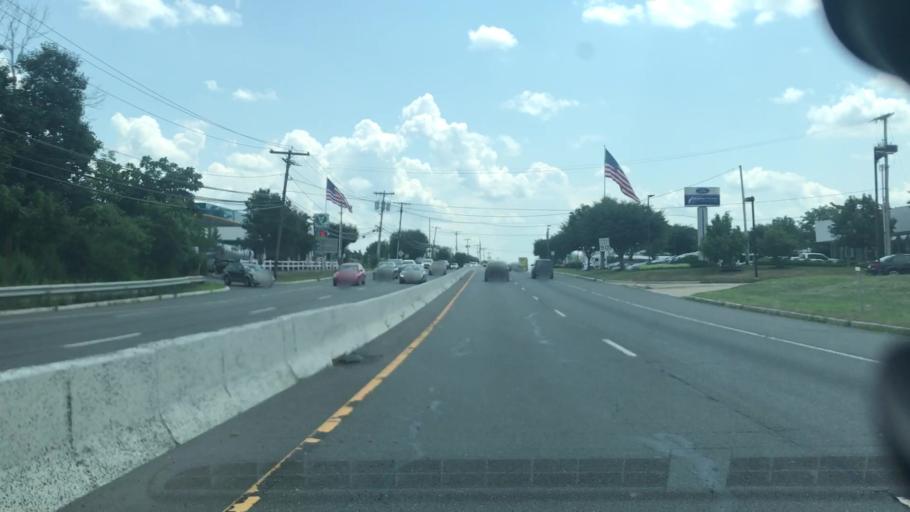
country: US
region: New Jersey
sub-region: Hunterdon County
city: Flemington
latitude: 40.4897
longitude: -74.8624
